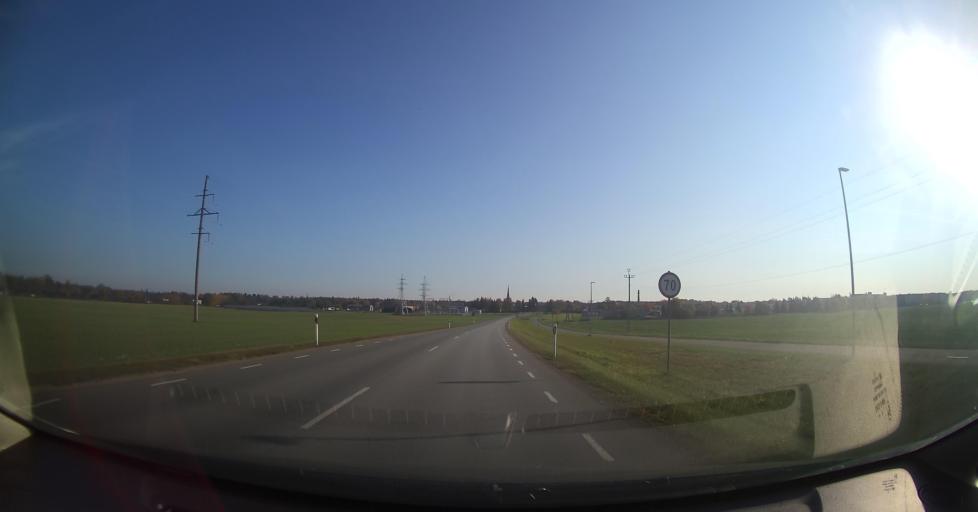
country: EE
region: Harju
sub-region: Raasiku vald
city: Raasiku
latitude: 59.1879
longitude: 25.1493
